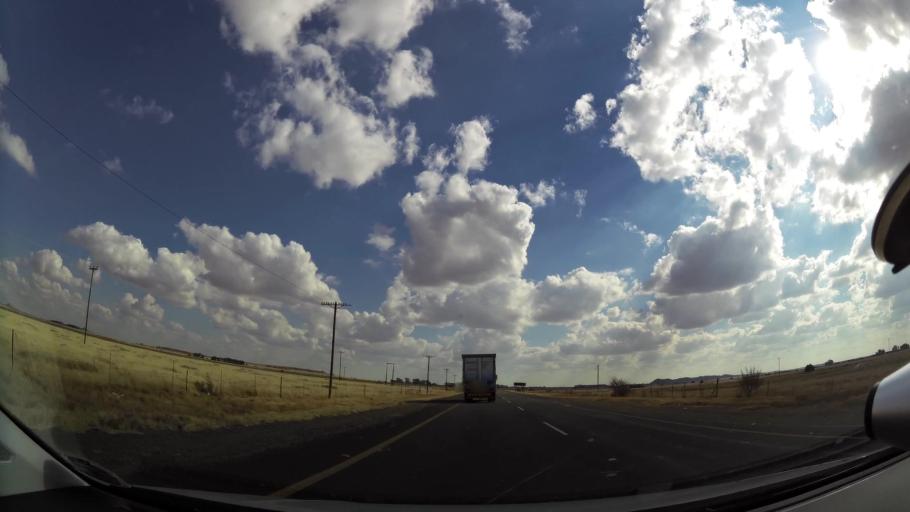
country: ZA
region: Orange Free State
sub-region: Xhariep District Municipality
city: Koffiefontein
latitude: -29.1264
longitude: 25.4711
